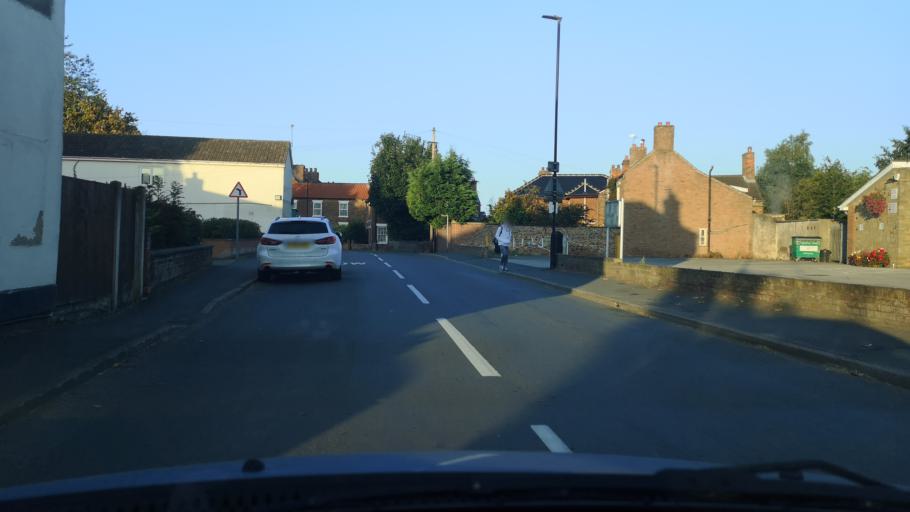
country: GB
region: England
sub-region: North Lincolnshire
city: Crowle
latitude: 53.6094
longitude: -0.8323
